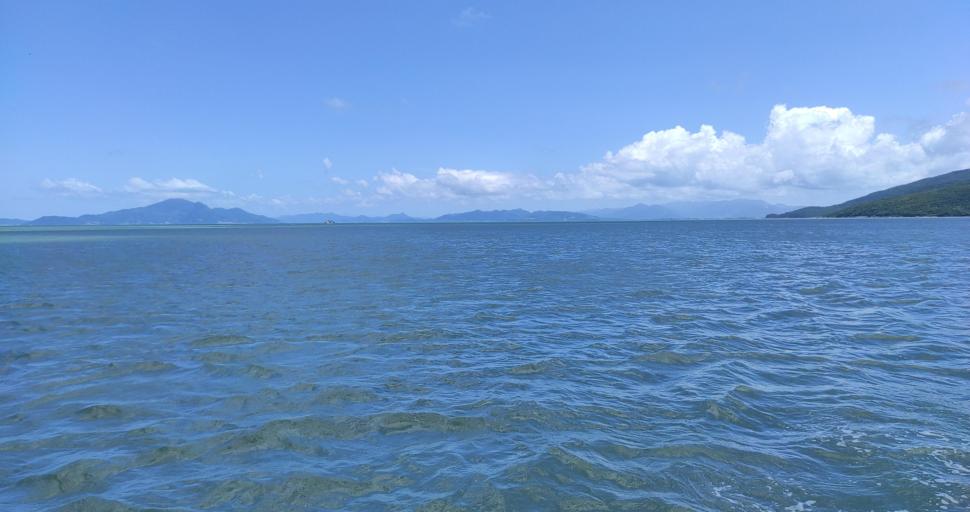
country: BR
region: Santa Catarina
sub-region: Porto Belo
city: Porto Belo
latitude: -27.1835
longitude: -48.5271
